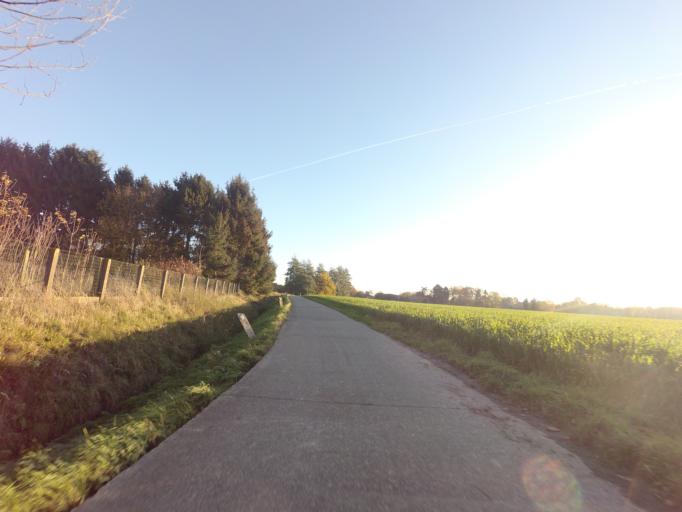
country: BE
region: Flanders
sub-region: Provincie Vlaams-Brabant
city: Zemst
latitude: 50.9892
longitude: 4.4532
